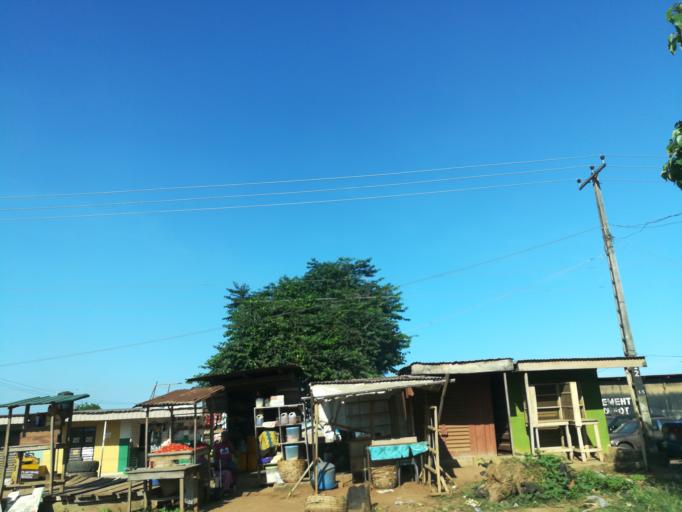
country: NG
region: Lagos
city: Ikorodu
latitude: 6.5672
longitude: 3.5342
